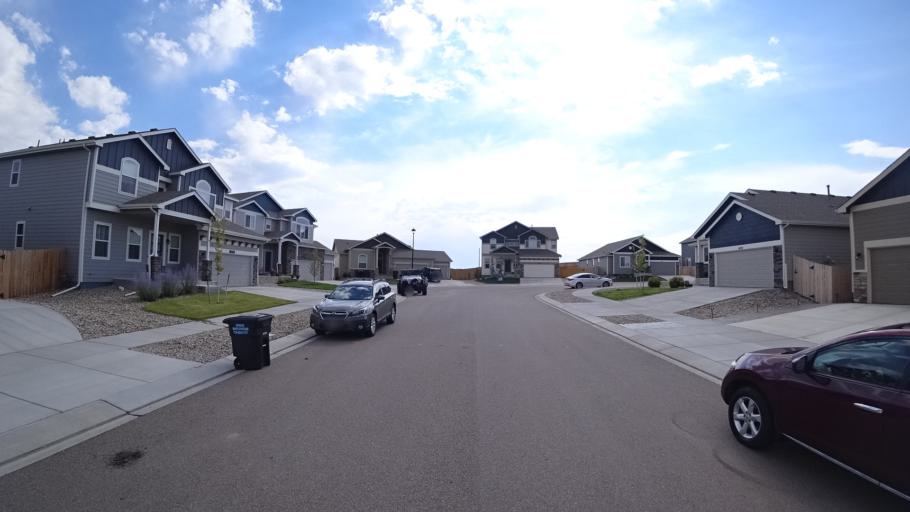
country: US
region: Colorado
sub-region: El Paso County
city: Cimarron Hills
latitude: 38.9215
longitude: -104.6815
